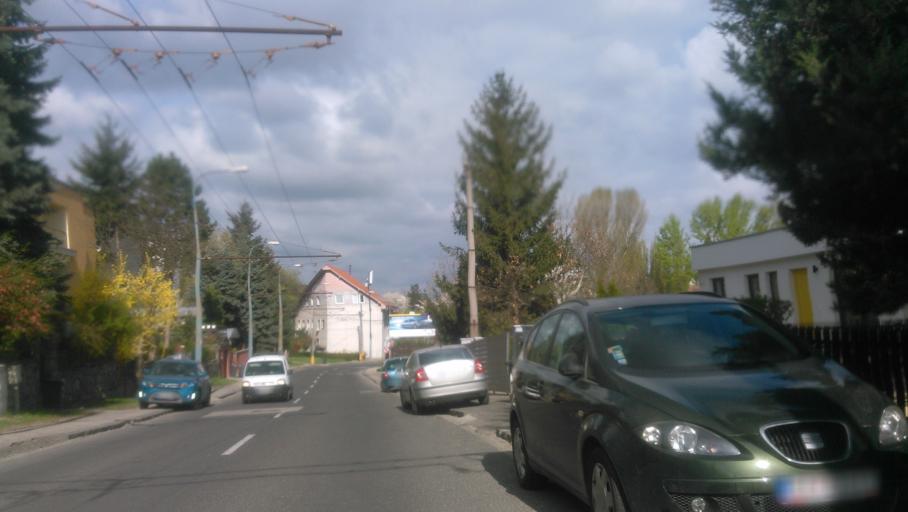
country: SK
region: Bratislavsky
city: Bratislava
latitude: 48.1619
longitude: 17.0833
